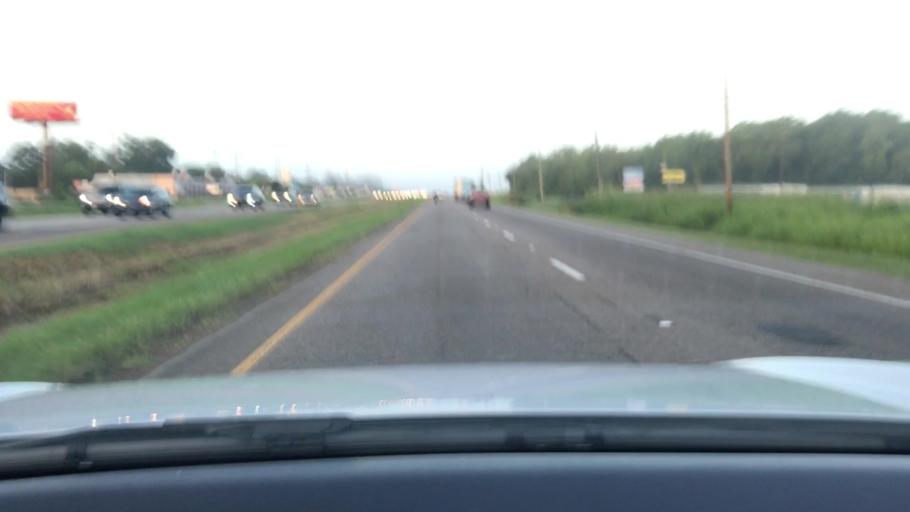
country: US
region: Louisiana
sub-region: West Baton Rouge Parish
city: Brusly
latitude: 30.4118
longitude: -91.2266
